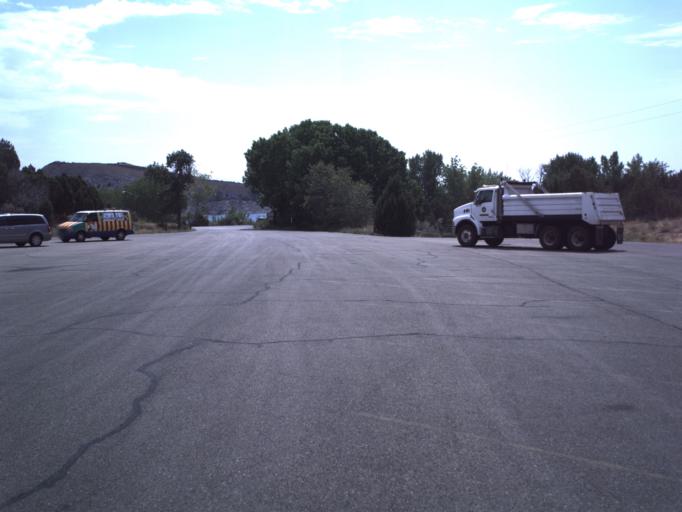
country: US
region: Utah
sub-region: Uintah County
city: Maeser
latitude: 40.5161
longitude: -109.5408
